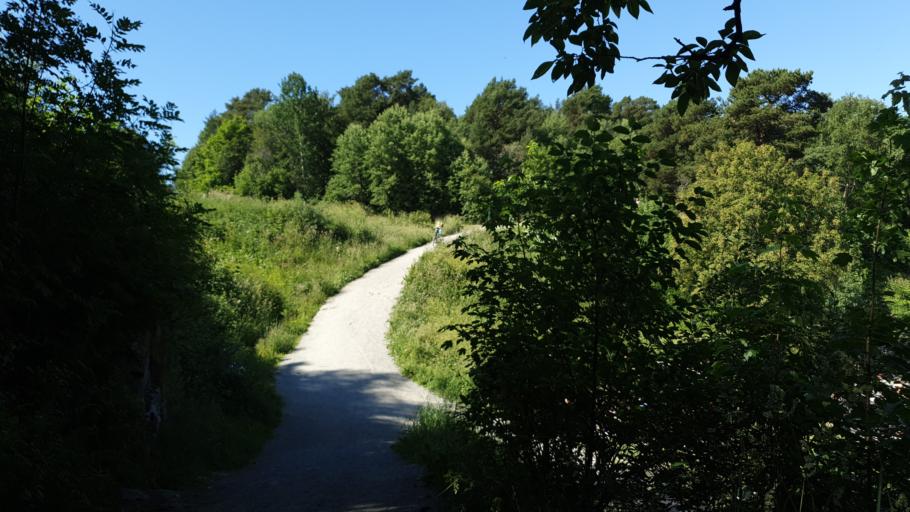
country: NO
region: Sor-Trondelag
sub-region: Trondheim
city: Trondheim
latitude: 63.4444
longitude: 10.4680
